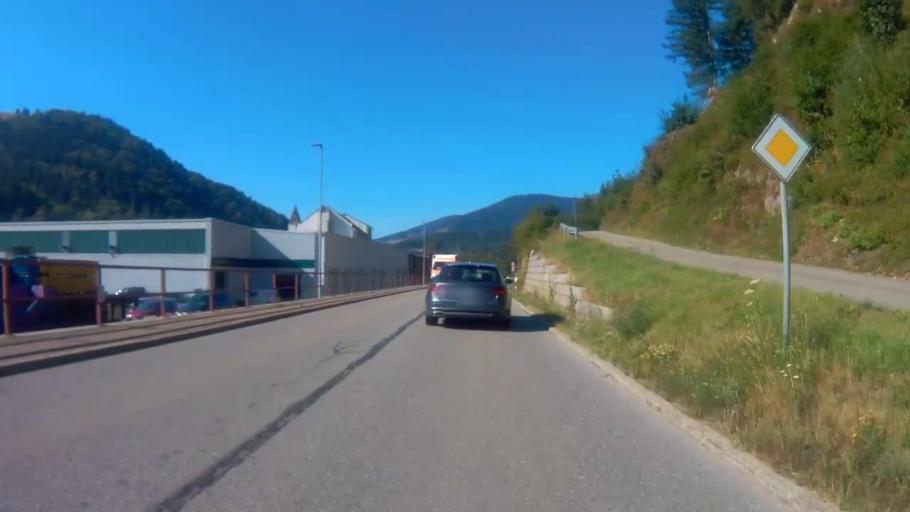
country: DE
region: Baden-Wuerttemberg
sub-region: Freiburg Region
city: Schonau im Schwarzwald
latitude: 47.7789
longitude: 7.8938
